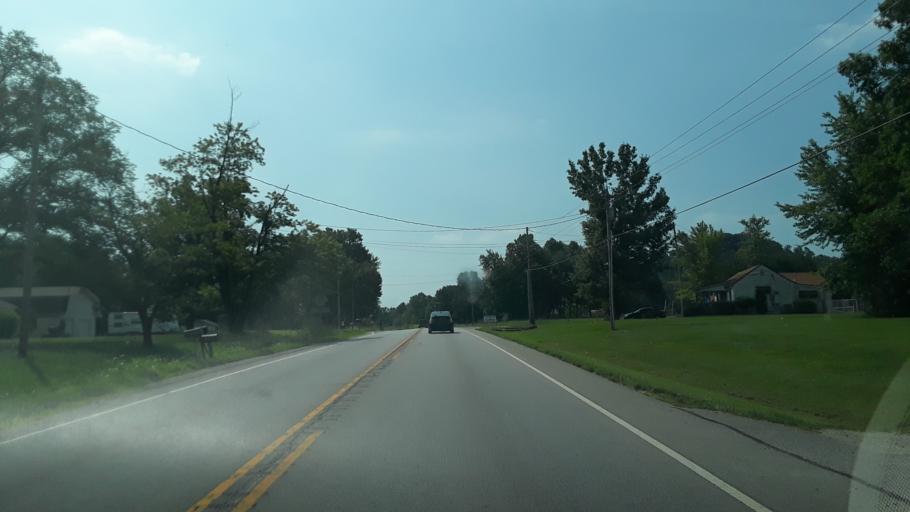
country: US
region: Indiana
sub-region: Clark County
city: Sellersburg
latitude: 38.4401
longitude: -85.8221
